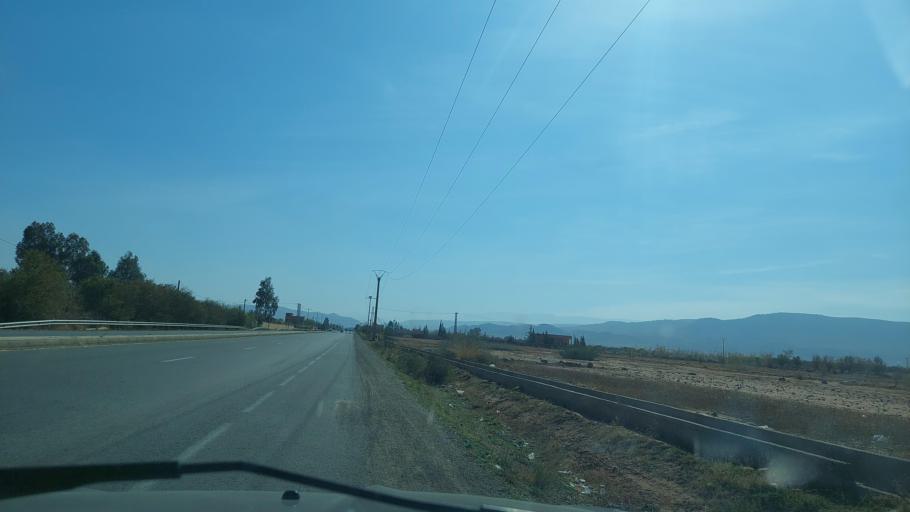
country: MA
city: Sidi Abdallah Ghiat
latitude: 31.5648
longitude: -7.7184
